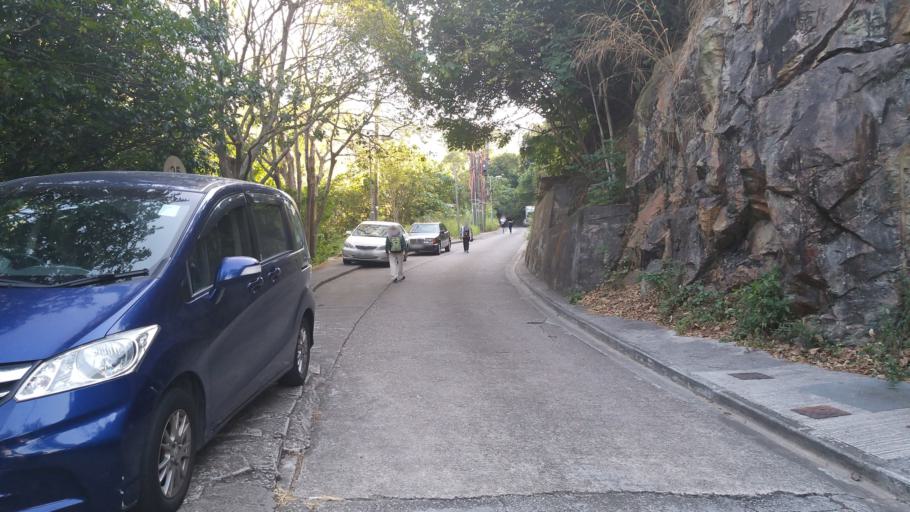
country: HK
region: Tuen Mun
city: Tuen Mun
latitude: 22.4073
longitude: 113.9855
